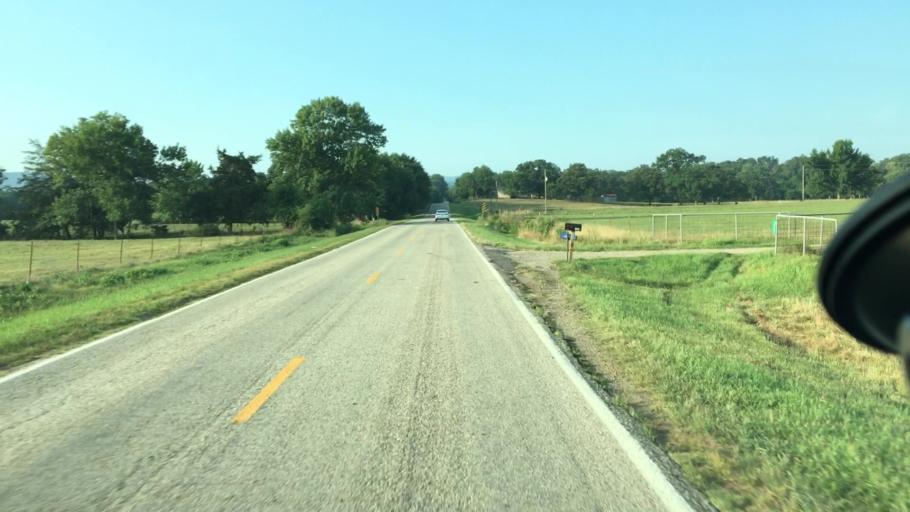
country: US
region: Arkansas
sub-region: Logan County
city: Paris
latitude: 35.3209
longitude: -93.6323
